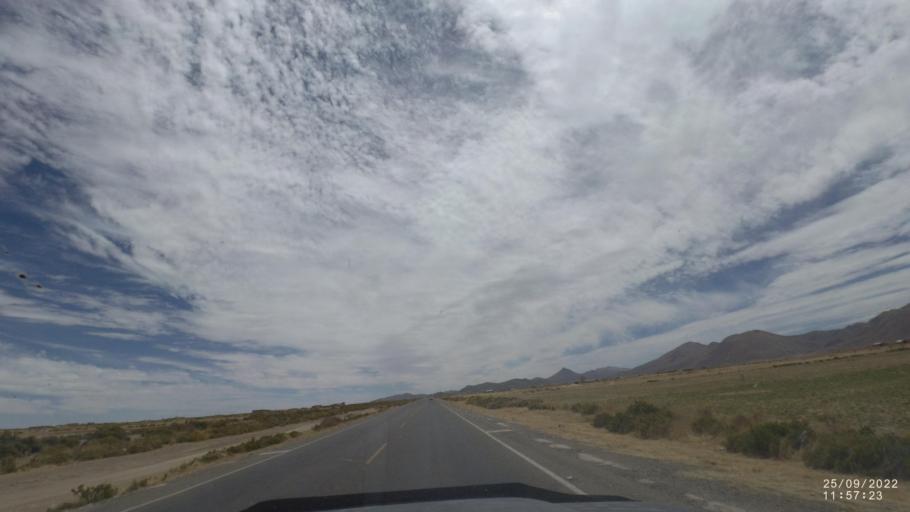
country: BO
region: Oruro
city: Challapata
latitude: -18.8235
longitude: -66.8272
